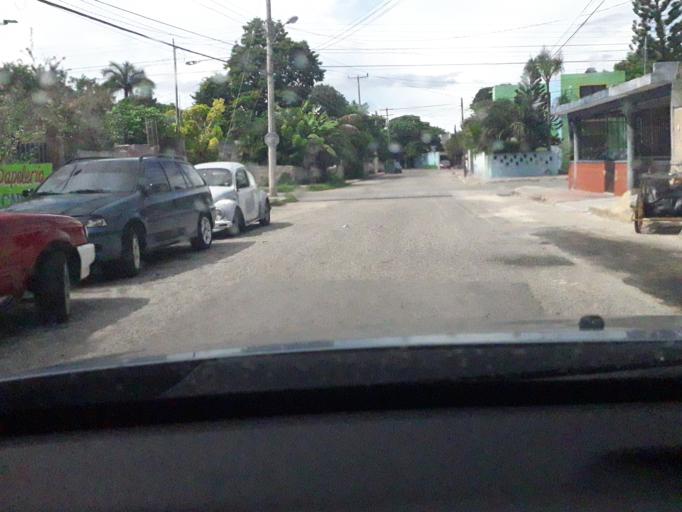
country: MX
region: Yucatan
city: Merida
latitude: 20.9660
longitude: -89.6592
